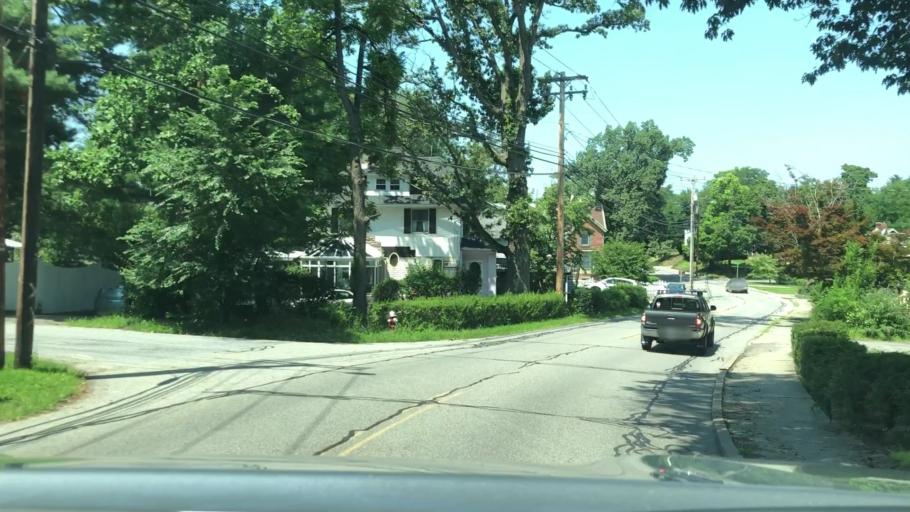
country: US
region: New York
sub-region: Dutchess County
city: Beacon
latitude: 41.4996
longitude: -73.9717
